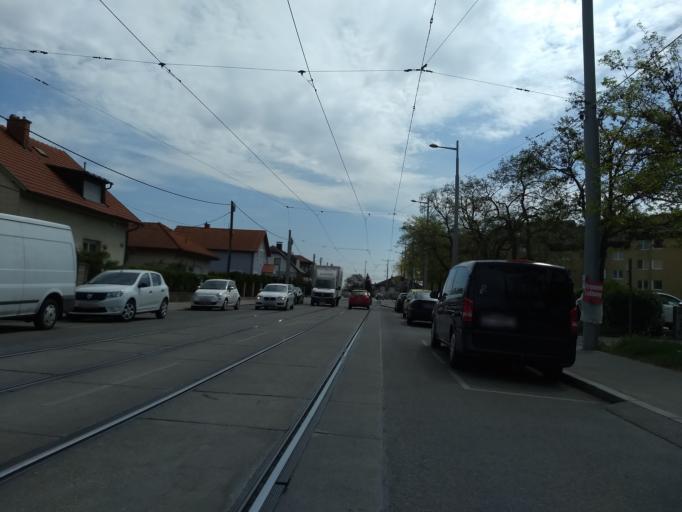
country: AT
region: Lower Austria
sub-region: Politischer Bezirk Wien-Umgebung
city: Gerasdorf bei Wien
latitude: 48.2375
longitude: 16.4865
